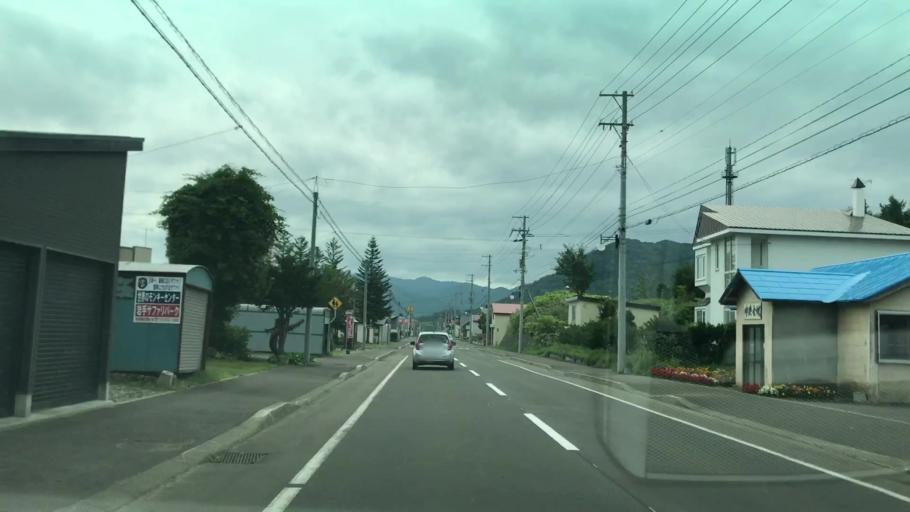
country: JP
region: Hokkaido
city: Yoichi
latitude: 43.0876
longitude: 140.8154
